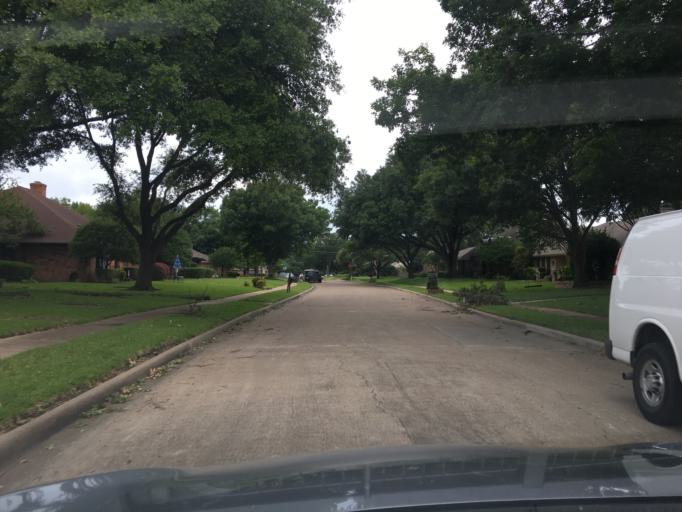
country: US
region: Texas
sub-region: Dallas County
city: Richardson
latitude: 32.9431
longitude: -96.7086
